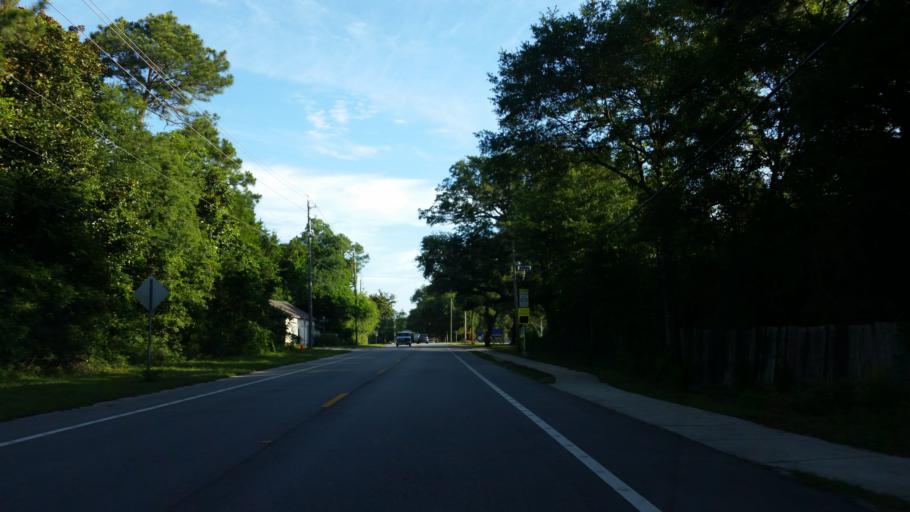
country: US
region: Florida
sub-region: Escambia County
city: Myrtle Grove
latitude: 30.3588
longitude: -87.3432
